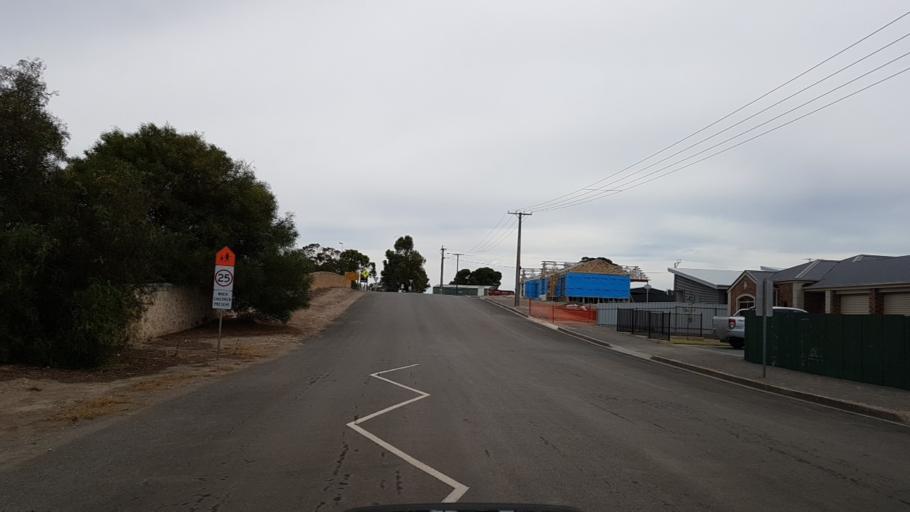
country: AU
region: South Australia
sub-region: Yorke Peninsula
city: Port Victoria
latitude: -34.7682
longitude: 137.5935
